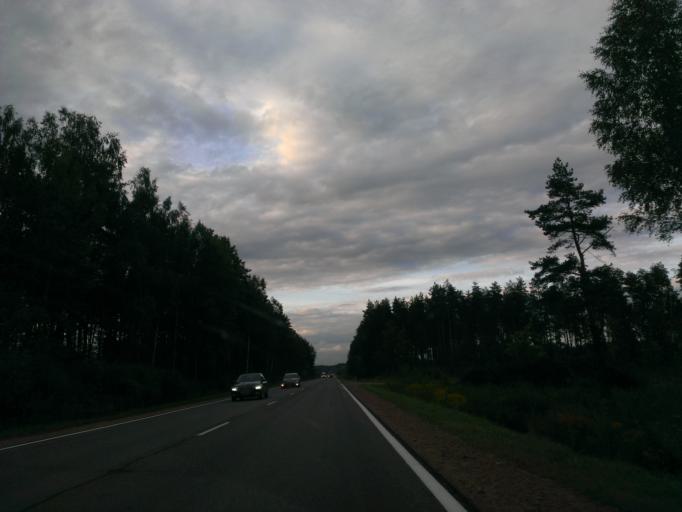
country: LV
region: Salaspils
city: Salaspils
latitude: 56.8900
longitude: 24.4073
